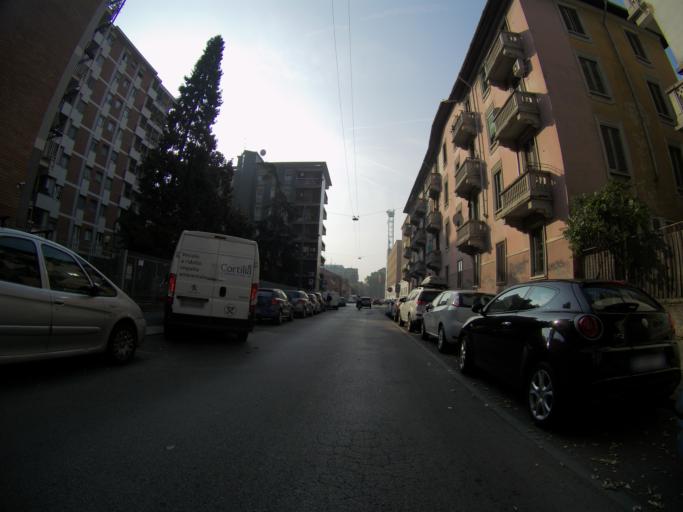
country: IT
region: Lombardy
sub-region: Citta metropolitana di Milano
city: Milano
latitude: 45.4732
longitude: 9.2195
